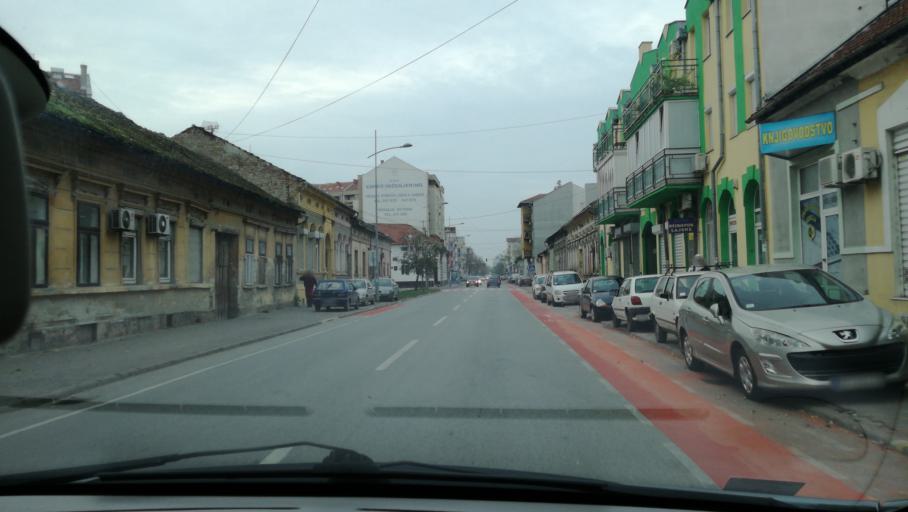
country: RS
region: Autonomna Pokrajina Vojvodina
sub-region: Juznobacki Okrug
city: Novi Sad
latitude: 45.2614
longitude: 19.8415
